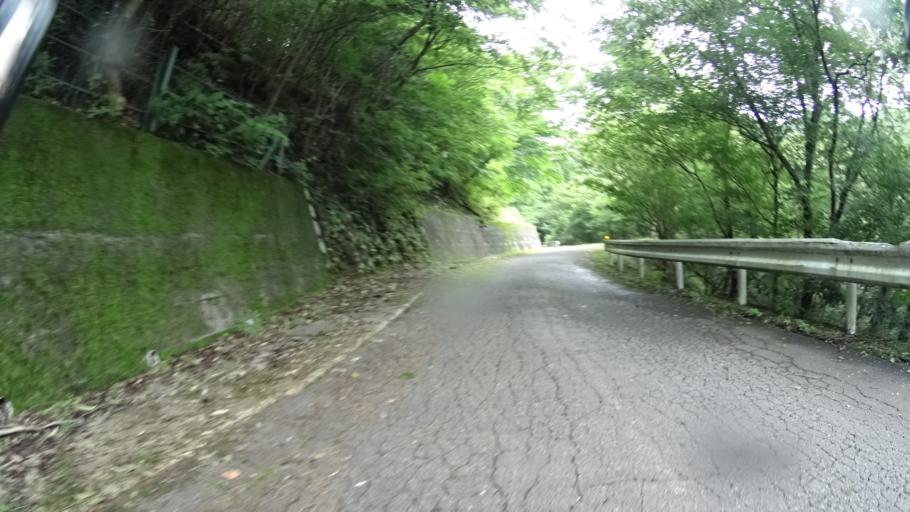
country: JP
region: Saitama
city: Chichibu
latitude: 35.8914
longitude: 139.1318
